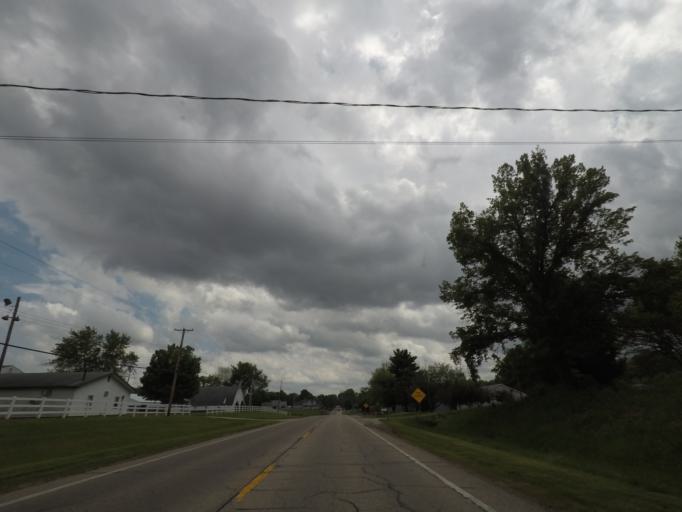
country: US
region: Illinois
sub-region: De Witt County
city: Clinton
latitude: 40.1635
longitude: -88.9605
